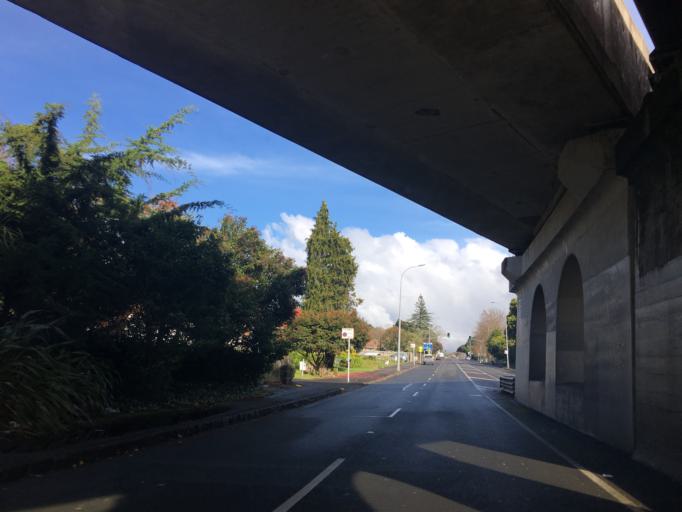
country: NZ
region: Auckland
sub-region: Auckland
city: Auckland
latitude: -36.8761
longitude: 174.7318
